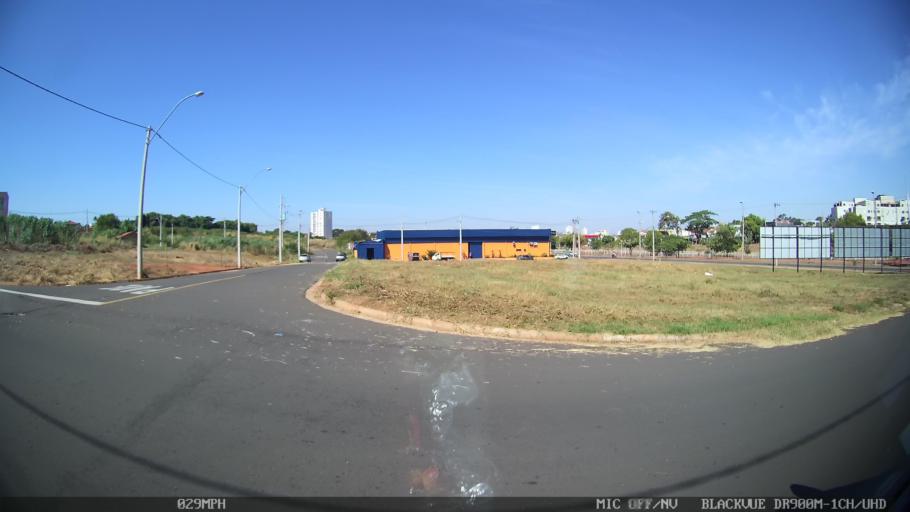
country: BR
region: Sao Paulo
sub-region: Sao Jose Do Rio Preto
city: Sao Jose do Rio Preto
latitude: -20.7831
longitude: -49.3786
